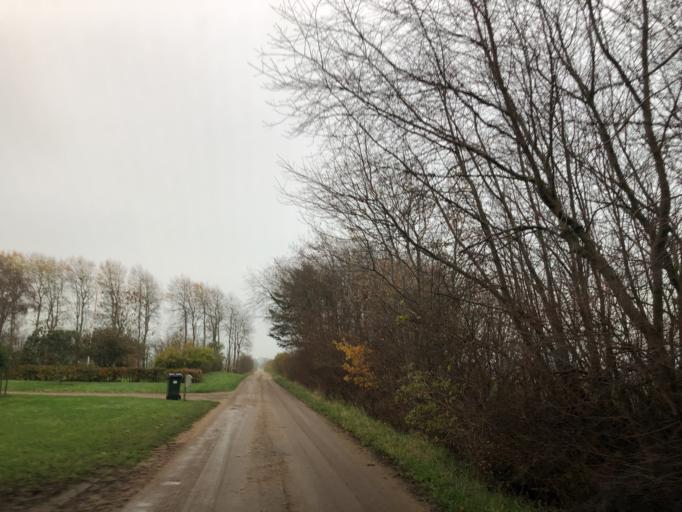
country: DK
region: Central Jutland
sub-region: Herning Kommune
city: Vildbjerg
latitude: 56.2125
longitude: 8.7270
